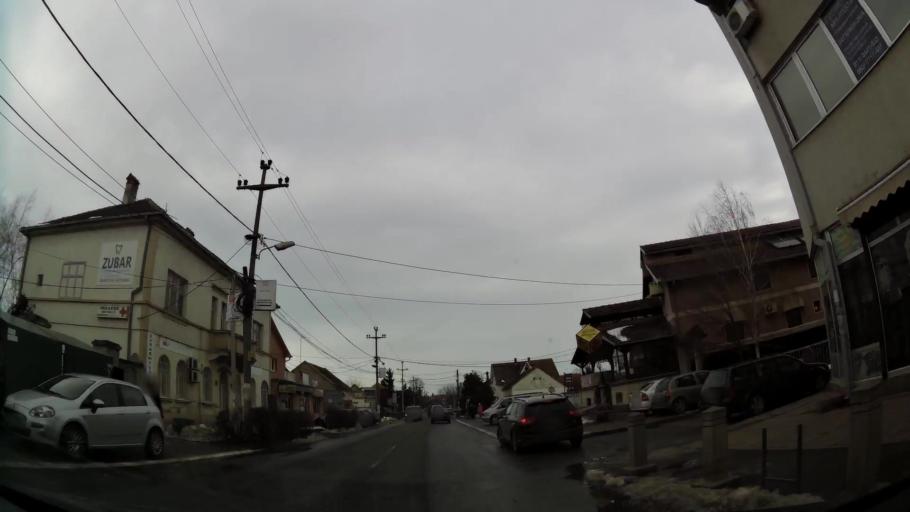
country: RS
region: Central Serbia
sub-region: Belgrade
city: Surcin
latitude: 44.7914
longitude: 20.2698
